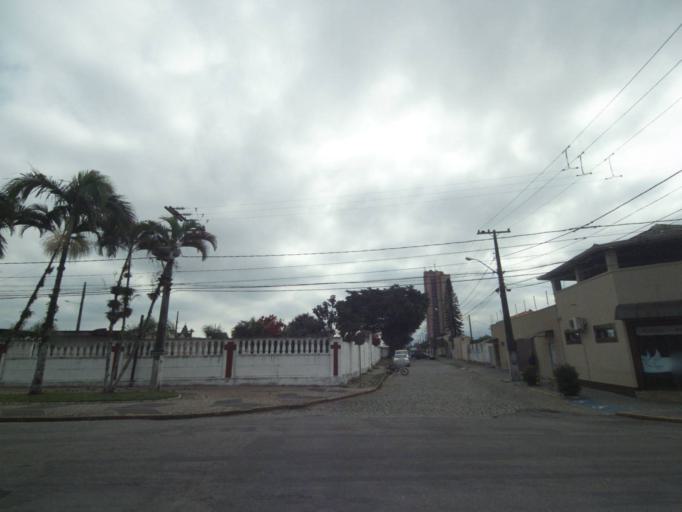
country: BR
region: Parana
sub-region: Paranagua
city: Paranagua
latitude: -25.5213
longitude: -48.5147
